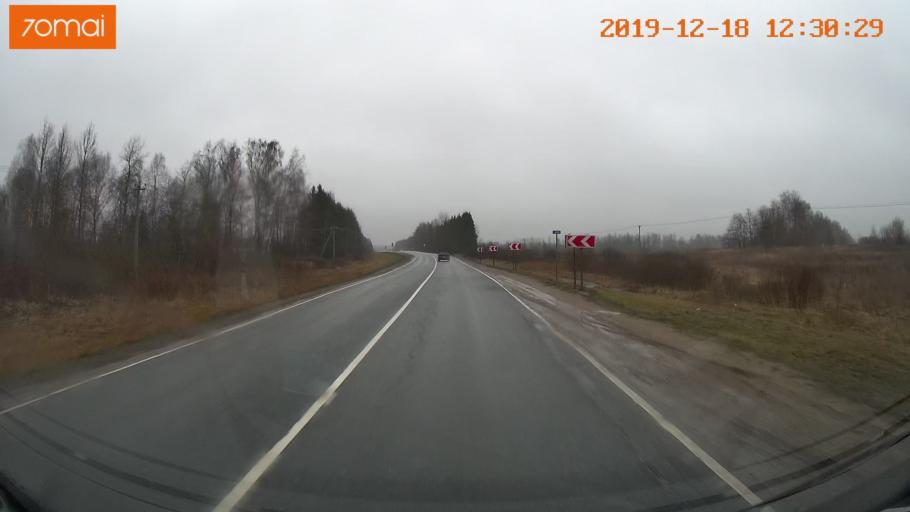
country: RU
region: Moskovskaya
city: Novopetrovskoye
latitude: 56.0897
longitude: 36.5326
